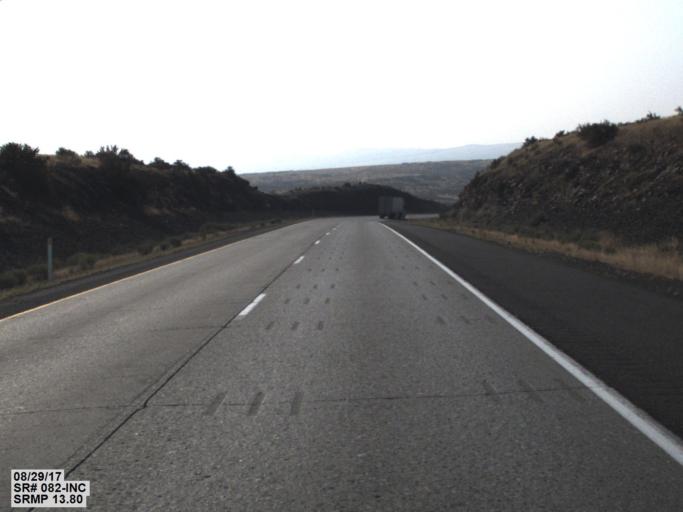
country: US
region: Washington
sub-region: Kittitas County
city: Kittitas
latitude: 46.8165
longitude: -120.3557
